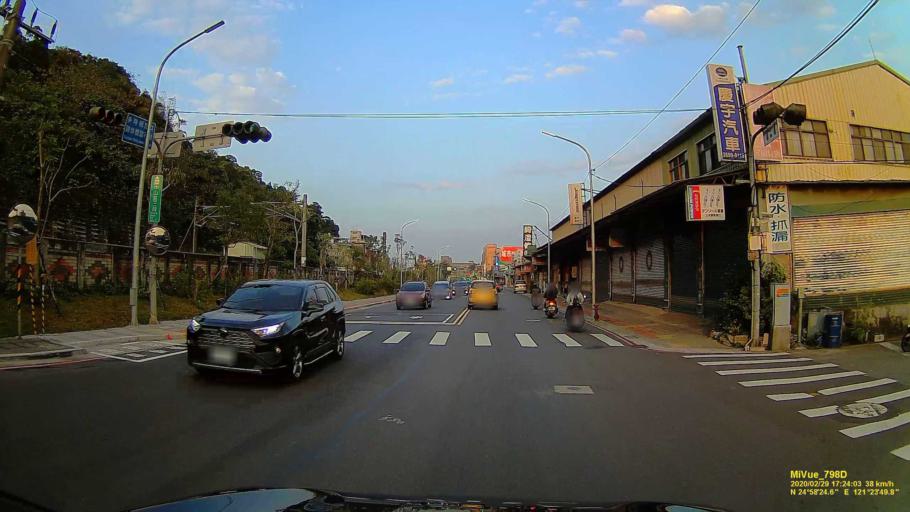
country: TW
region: Taiwan
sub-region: Taoyuan
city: Taoyuan
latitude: 24.9735
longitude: 121.3973
